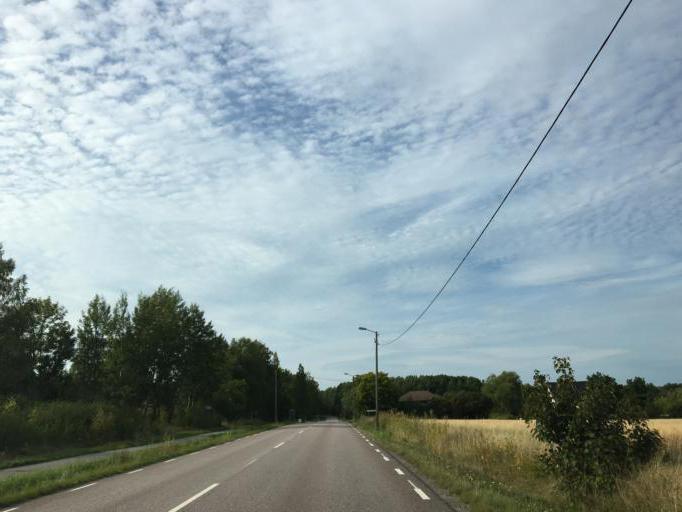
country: SE
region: Soedermanland
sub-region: Eskilstuna Kommun
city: Torshalla
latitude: 59.4438
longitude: 16.4516
